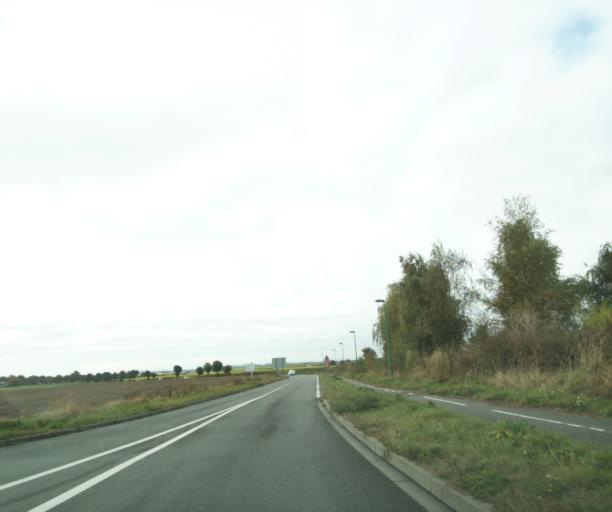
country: FR
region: Nord-Pas-de-Calais
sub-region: Departement du Nord
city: Vendeville
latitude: 50.5809
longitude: 3.0956
